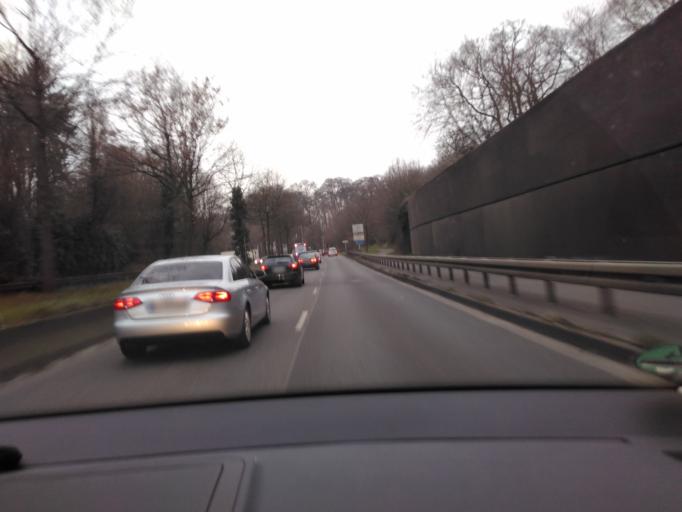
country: DE
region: North Rhine-Westphalia
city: Opladen
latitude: 51.0385
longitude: 7.0394
